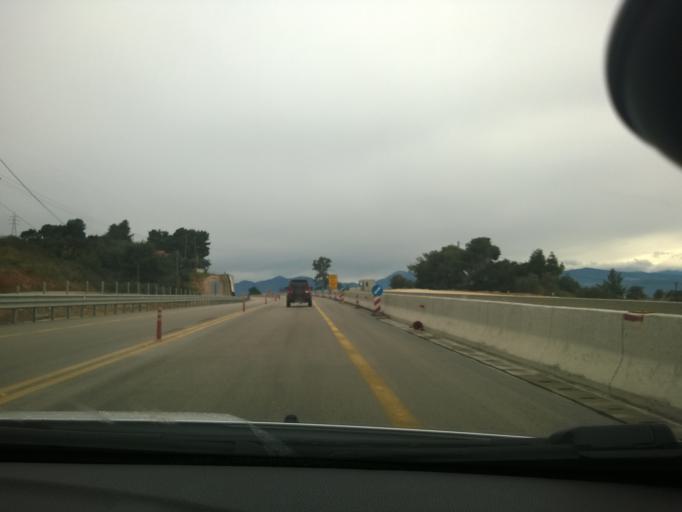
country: GR
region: West Greece
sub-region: Nomos Achaias
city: Kamarai
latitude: 38.3094
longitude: 21.9877
